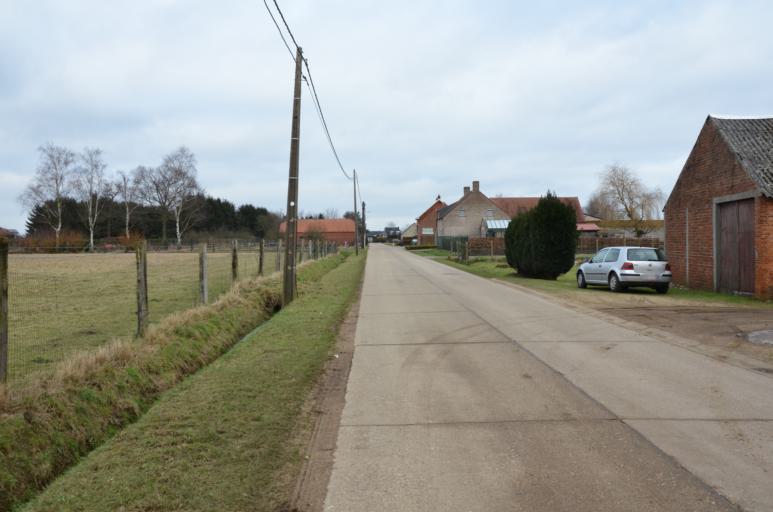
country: BE
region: Flanders
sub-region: Provincie Antwerpen
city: Lille
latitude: 51.2242
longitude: 4.8430
